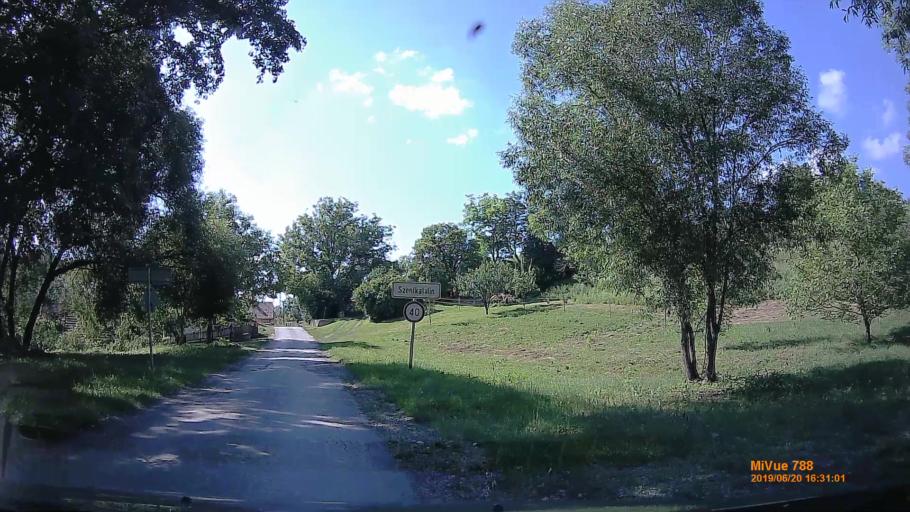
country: HU
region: Baranya
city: Buekkoesd
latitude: 46.1715
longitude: 18.0518
